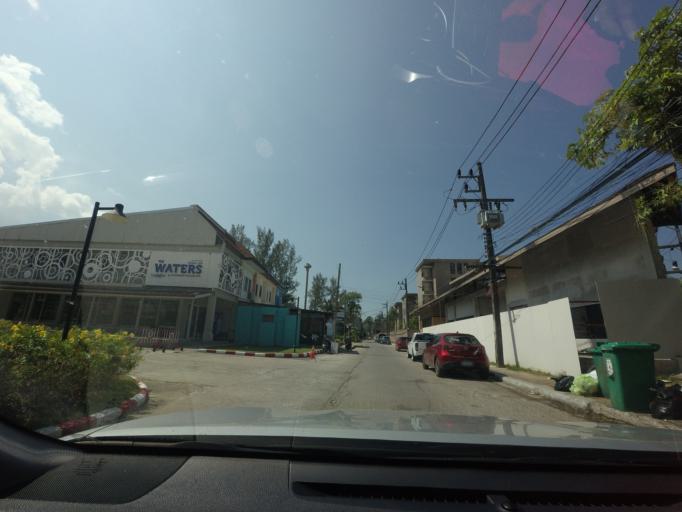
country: TH
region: Phangnga
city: Ban Khao Lak
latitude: 8.6651
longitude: 98.2478
